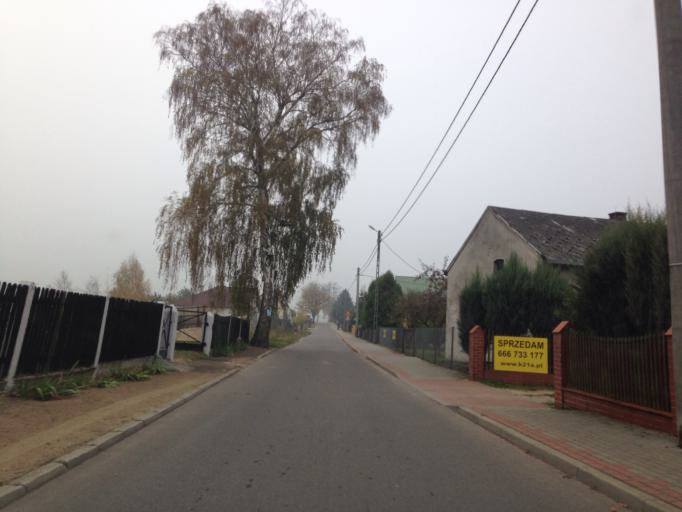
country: PL
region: Warmian-Masurian Voivodeship
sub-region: Powiat nowomiejski
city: Biskupiec
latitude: 53.5068
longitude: 19.3964
